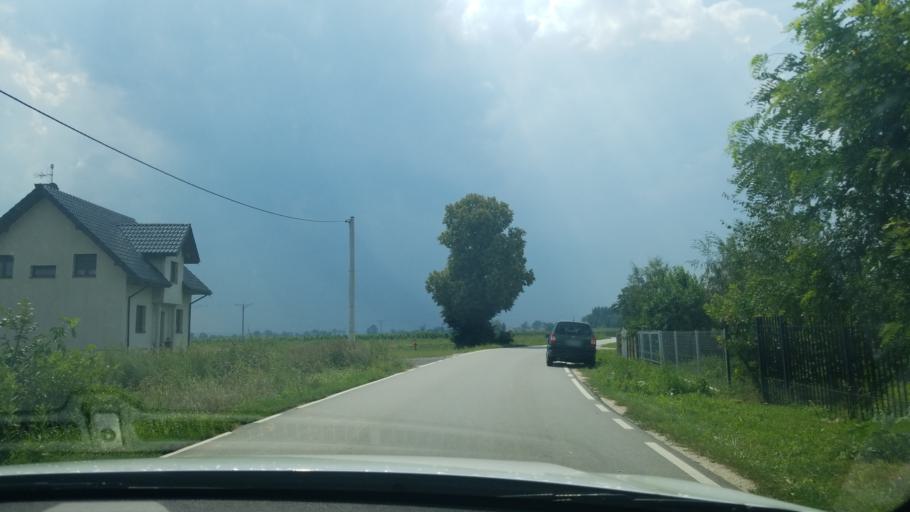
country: PL
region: Lesser Poland Voivodeship
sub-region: Powiat bochenski
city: Dziewin
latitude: 50.1141
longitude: 20.5171
